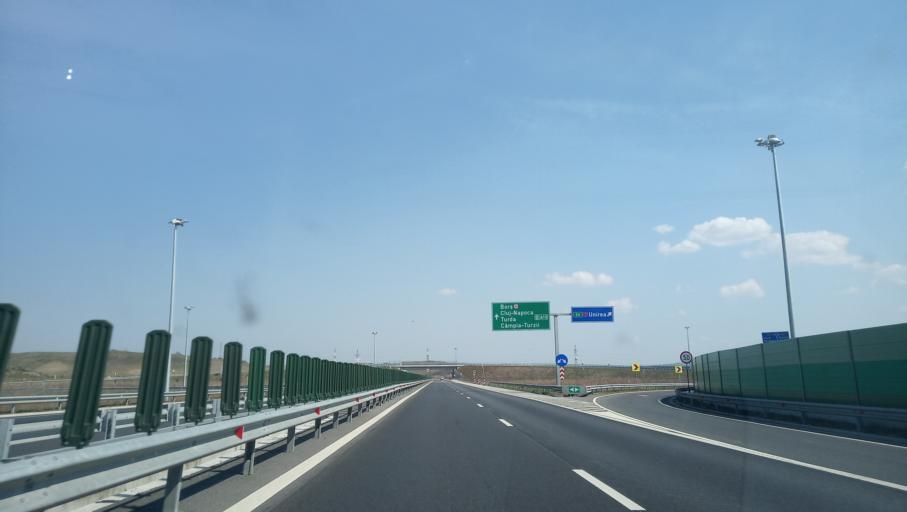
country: RO
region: Alba
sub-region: Comuna Unirea
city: Unirea
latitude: 46.3869
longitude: 23.7670
